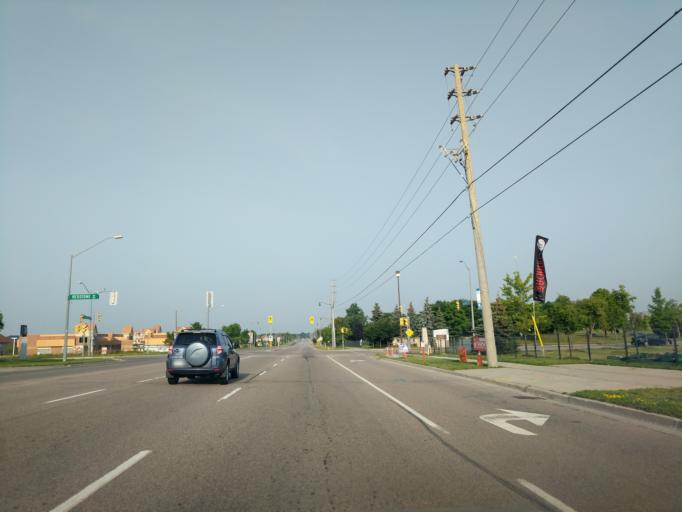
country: CA
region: Ontario
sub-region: York
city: Richmond Hill
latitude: 43.8975
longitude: -79.4001
